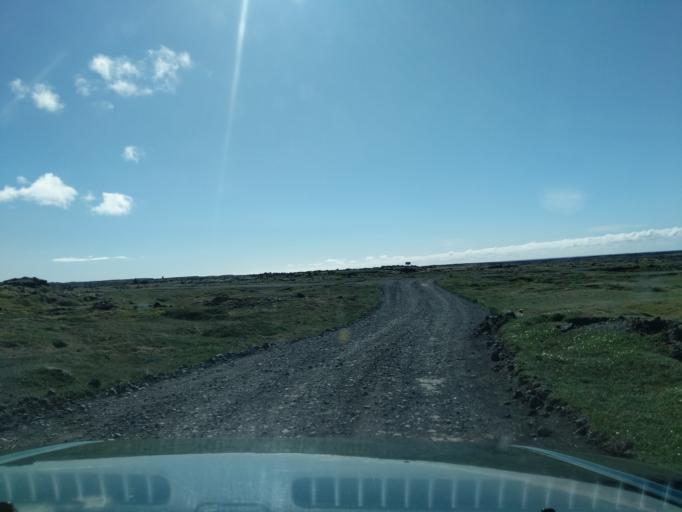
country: IS
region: West
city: Olafsvik
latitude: 64.8737
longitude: -24.0060
